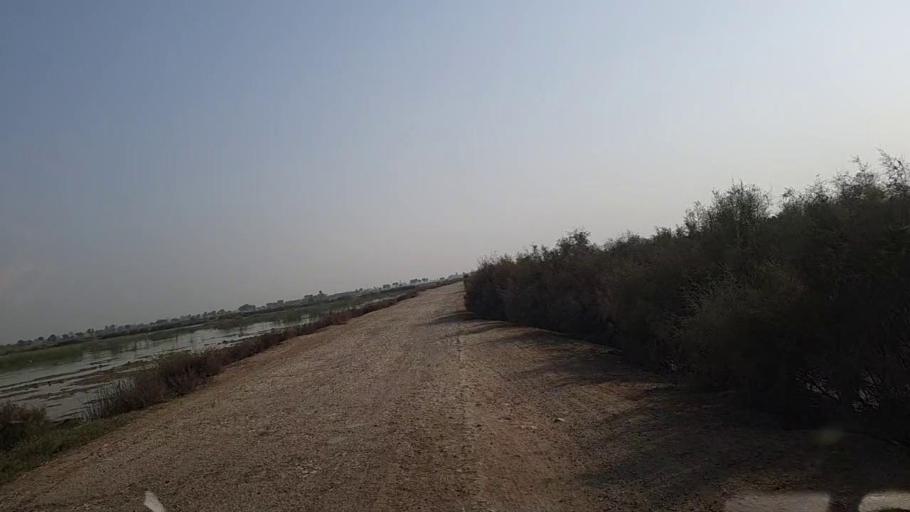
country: PK
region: Sindh
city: Kandhkot
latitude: 28.2925
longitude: 69.2532
